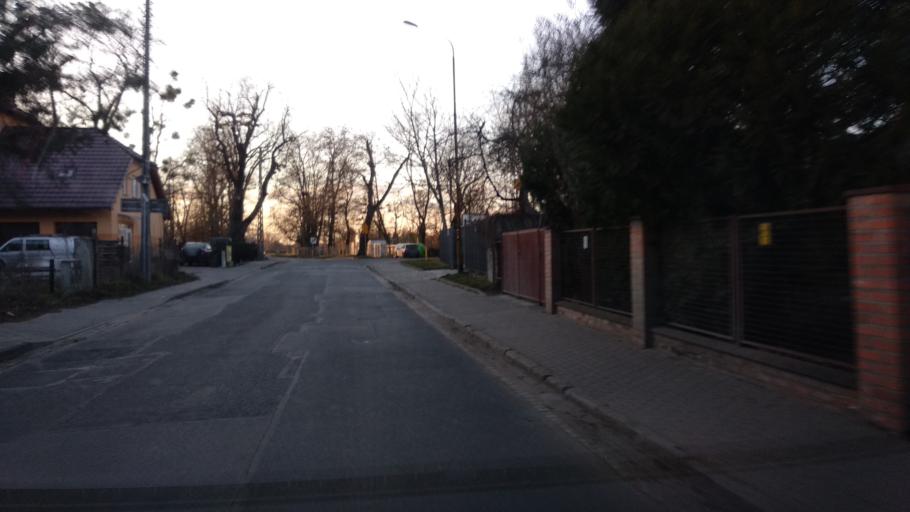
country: PL
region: Lower Silesian Voivodeship
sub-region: Powiat wroclawski
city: Zerniki Wroclawskie
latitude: 51.0637
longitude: 17.0739
